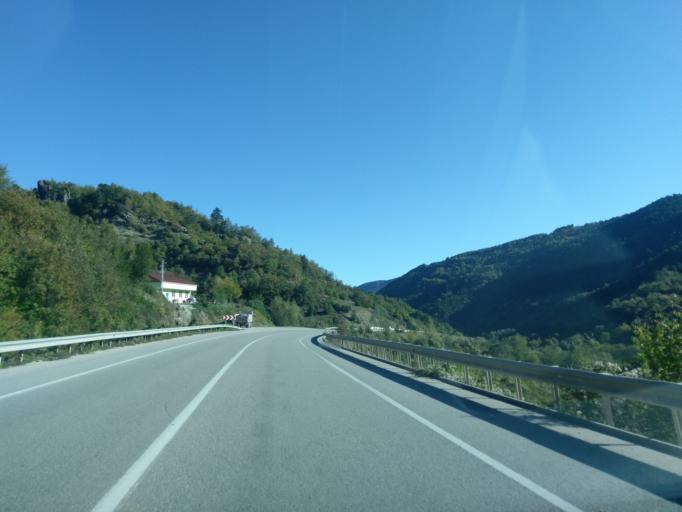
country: TR
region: Sinop
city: Erfelek
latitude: 41.7096
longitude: 34.9243
